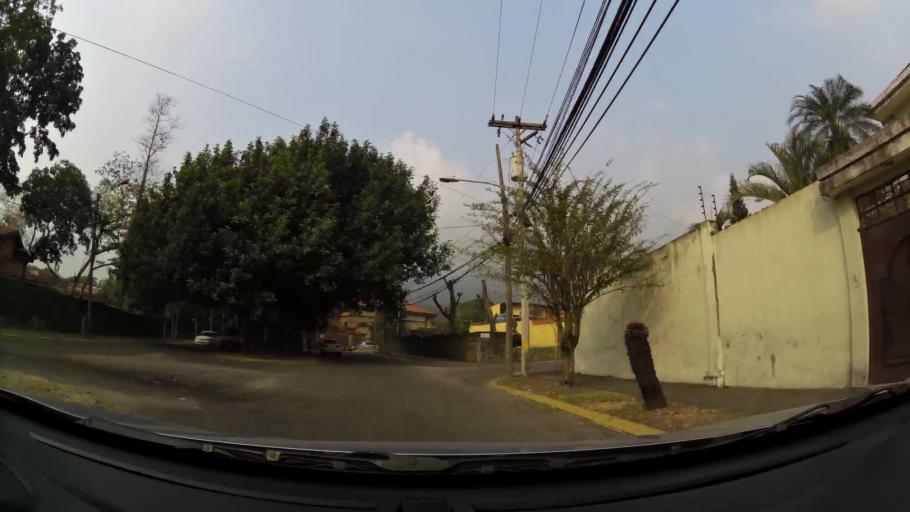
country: HN
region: Cortes
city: Armenta
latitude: 15.4893
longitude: -88.0389
